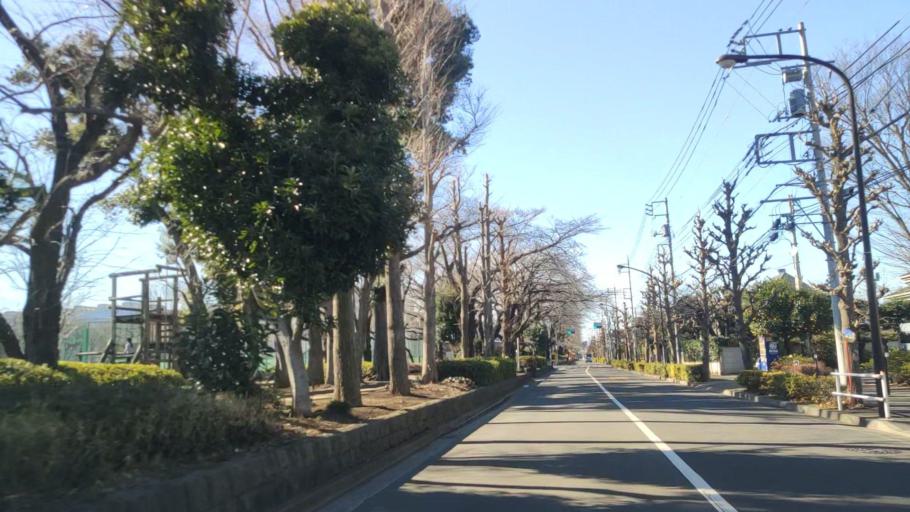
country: JP
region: Tokyo
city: Musashino
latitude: 35.7200
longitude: 139.5670
